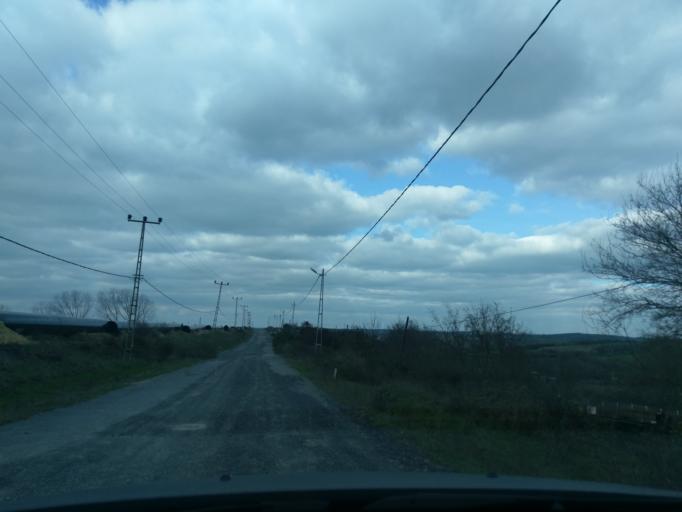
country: TR
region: Istanbul
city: Durusu
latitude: 41.2829
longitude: 28.6975
